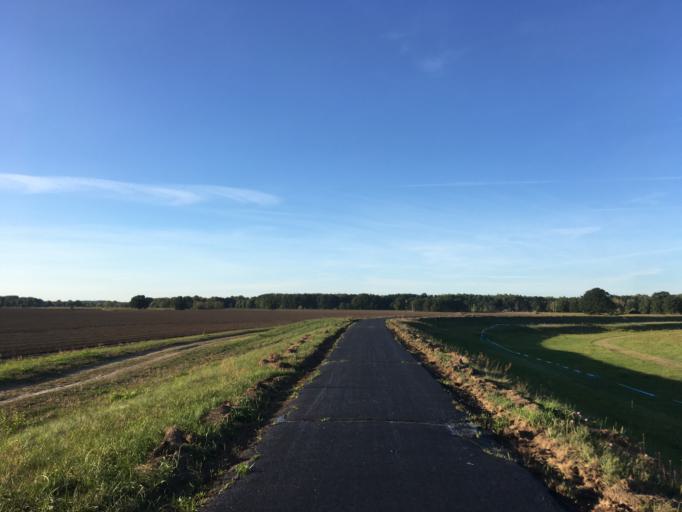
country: PL
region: Lubusz
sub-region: Powiat zarski
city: Trzebiel
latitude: 51.6800
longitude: 14.7362
